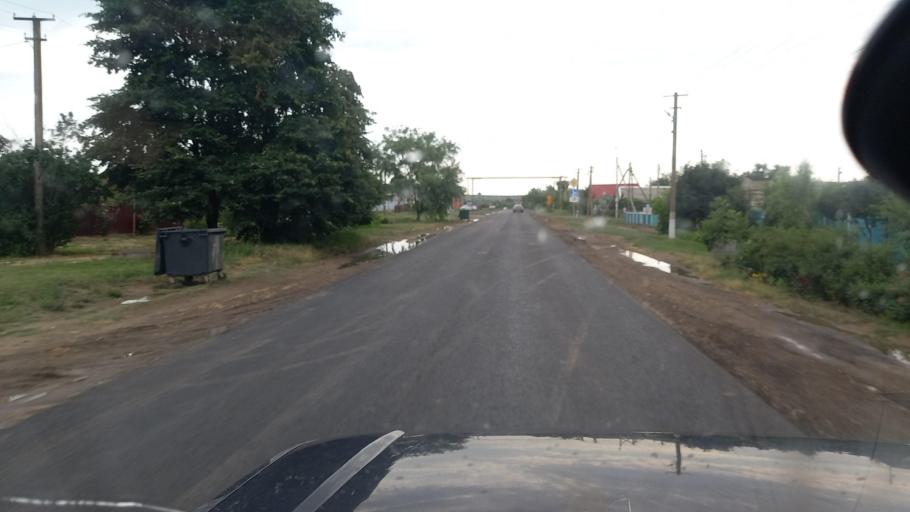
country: RU
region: Krasnodarskiy
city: Akhtanizovskaya
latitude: 45.3275
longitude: 37.1097
